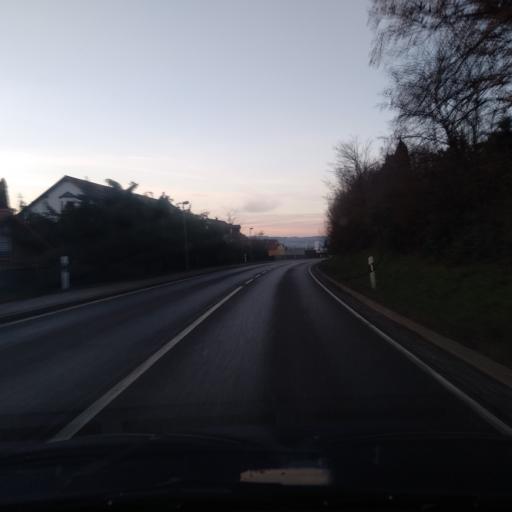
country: DE
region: Baden-Wuerttemberg
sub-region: Karlsruhe Region
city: Calw
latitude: 48.6984
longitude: 8.7648
